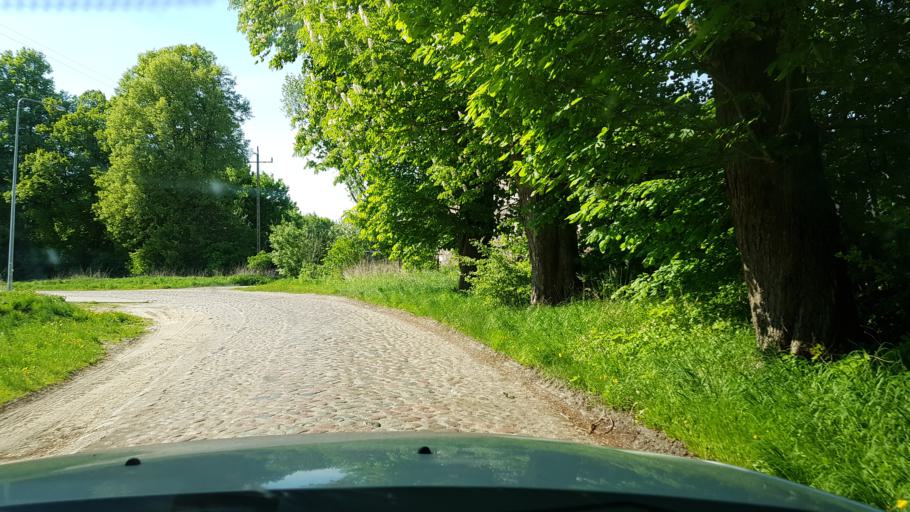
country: PL
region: West Pomeranian Voivodeship
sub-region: Powiat kolobrzeski
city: Goscino
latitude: 54.0072
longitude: 15.5920
